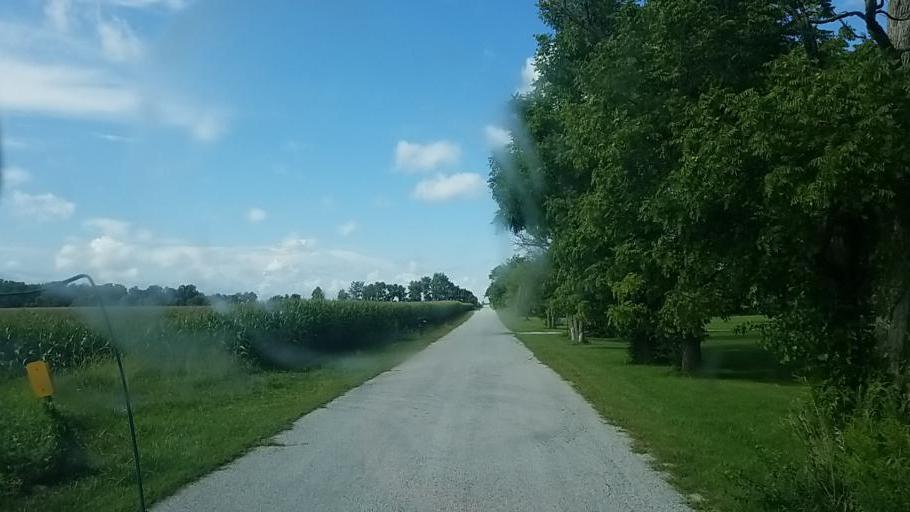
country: US
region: Ohio
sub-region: Hardin County
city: Kenton
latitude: 40.6729
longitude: -83.5476
